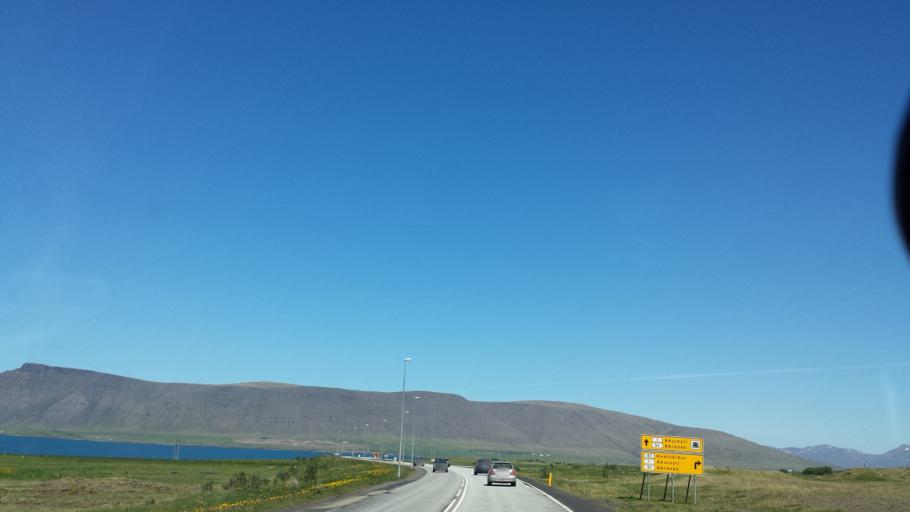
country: IS
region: Capital Region
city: Reykjavik
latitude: 64.2717
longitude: -21.8356
